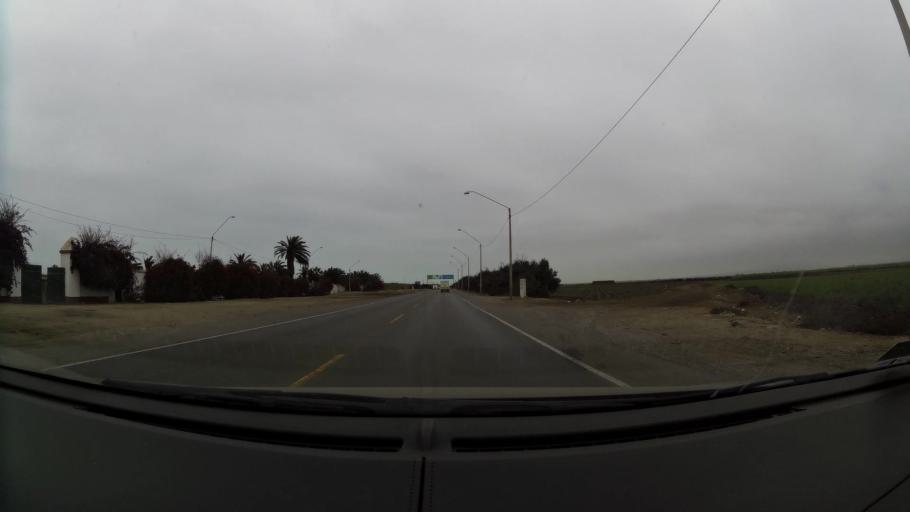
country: PE
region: La Libertad
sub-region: Provincia de Trujillo
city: Buenos Aires
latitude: -8.1360
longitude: -79.0599
